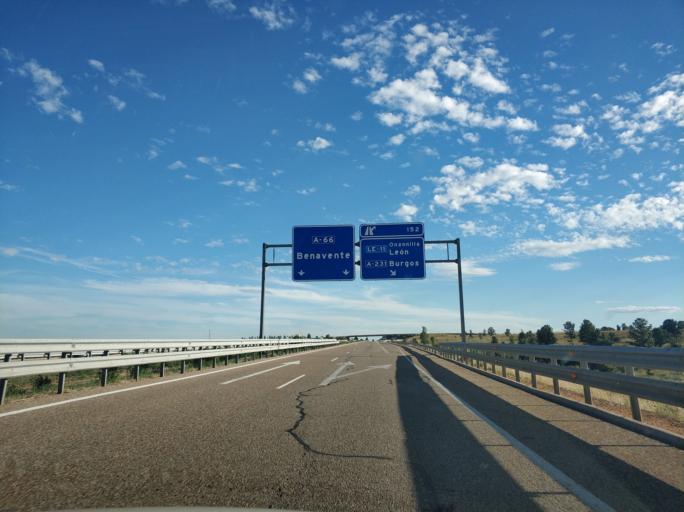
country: ES
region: Castille and Leon
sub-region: Provincia de Leon
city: Onzonilla
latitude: 42.5123
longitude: -5.5963
